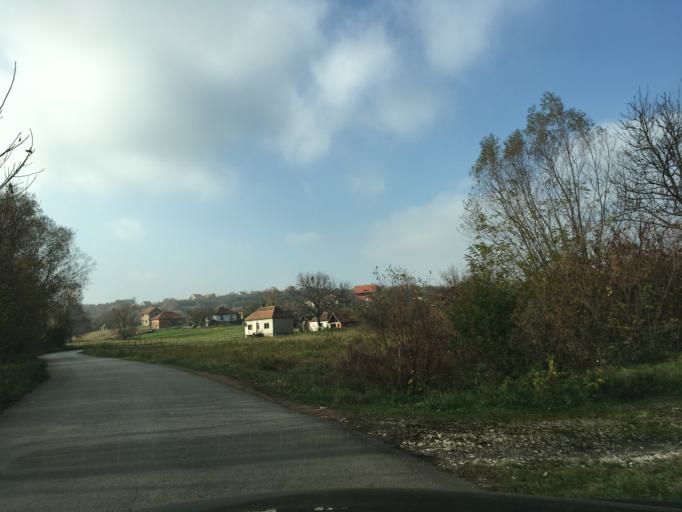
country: RS
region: Central Serbia
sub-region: Belgrade
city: Sopot
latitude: 44.4948
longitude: 20.5843
